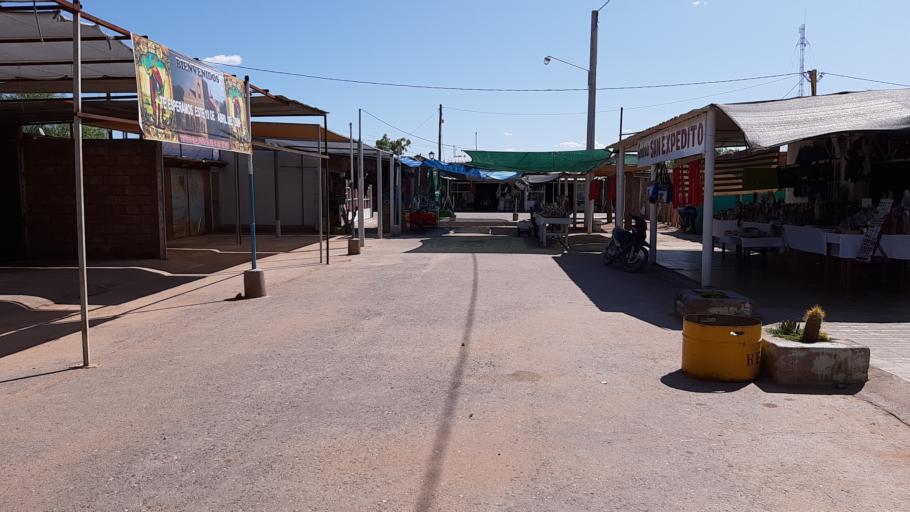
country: AR
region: San Juan
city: Caucete
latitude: -31.5885
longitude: -67.6570
